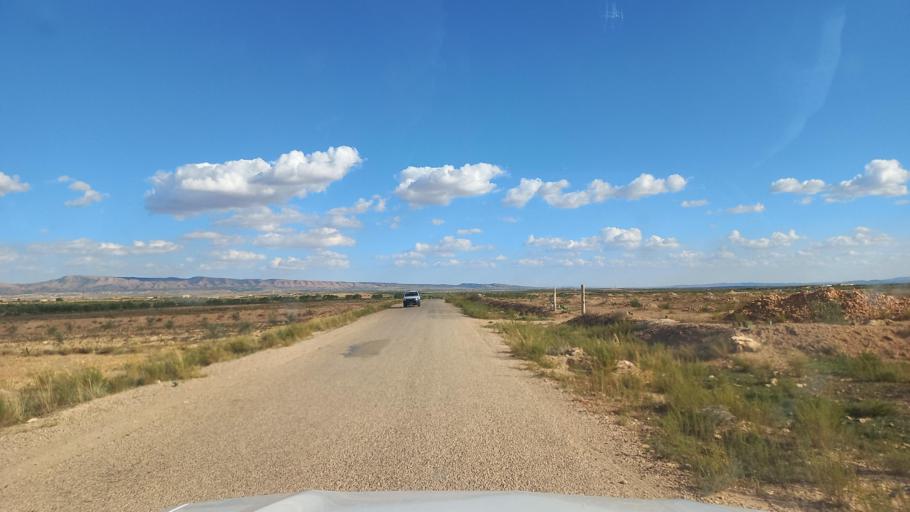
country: TN
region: Al Qasrayn
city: Sbiba
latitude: 35.3907
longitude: 9.0258
